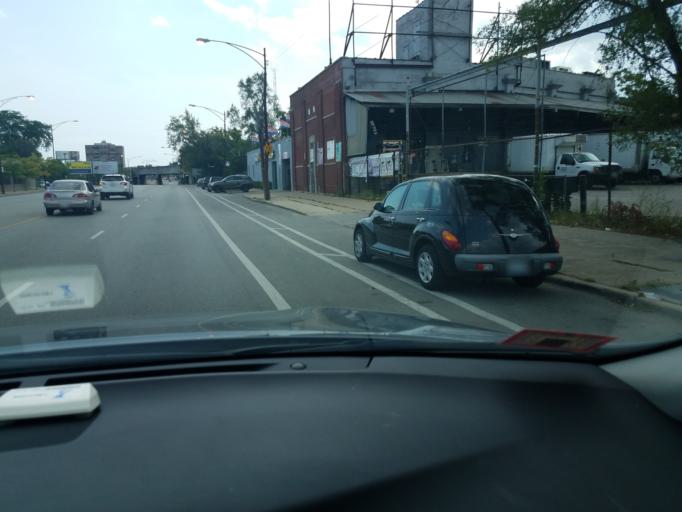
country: US
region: Illinois
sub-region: Cook County
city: Harwood Heights
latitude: 41.9738
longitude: -87.7661
